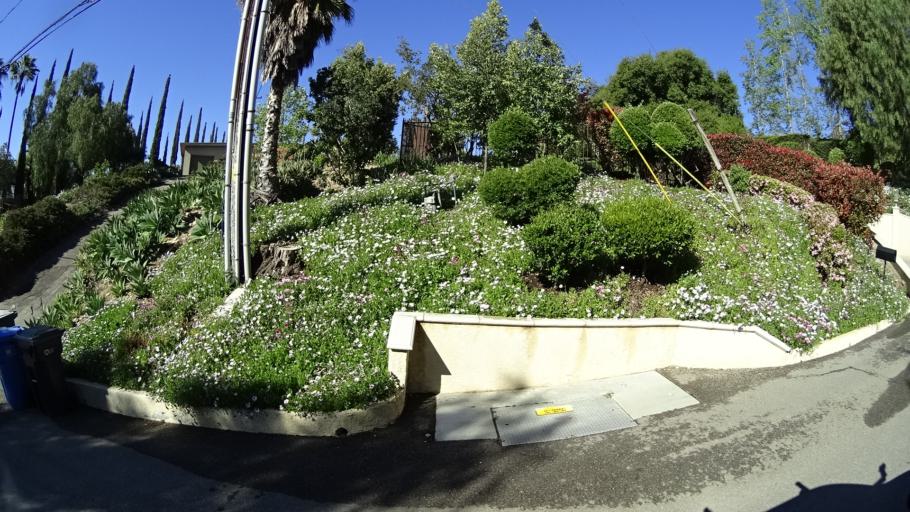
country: US
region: California
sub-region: Ventura County
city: Thousand Oaks
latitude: 34.1837
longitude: -118.8452
